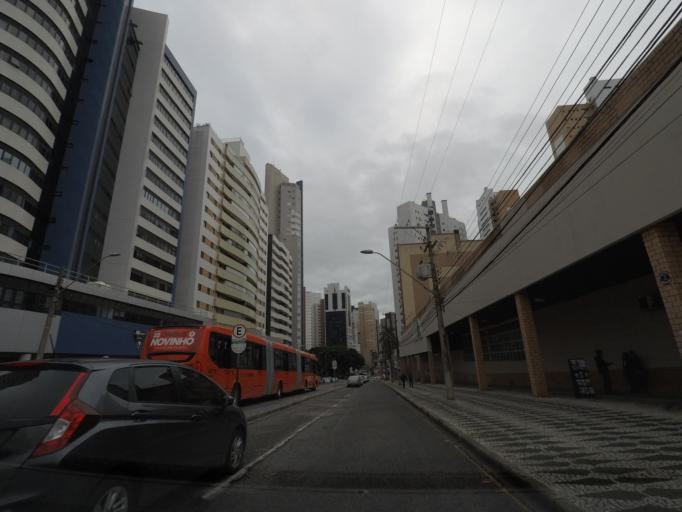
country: BR
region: Parana
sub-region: Curitiba
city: Curitiba
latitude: -25.4507
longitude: -49.2880
